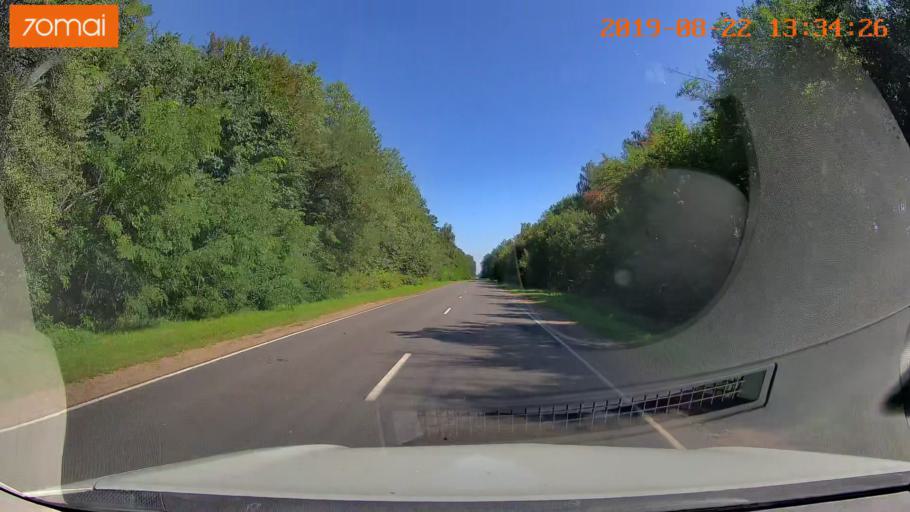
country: BY
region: Minsk
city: Staryya Darohi
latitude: 53.2153
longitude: 28.2412
